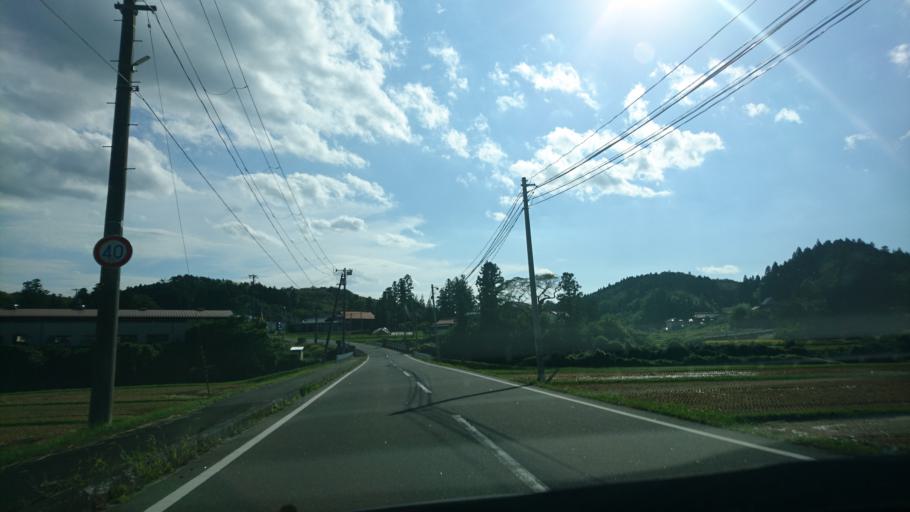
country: JP
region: Iwate
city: Ichinoseki
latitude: 38.8710
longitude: 141.1116
